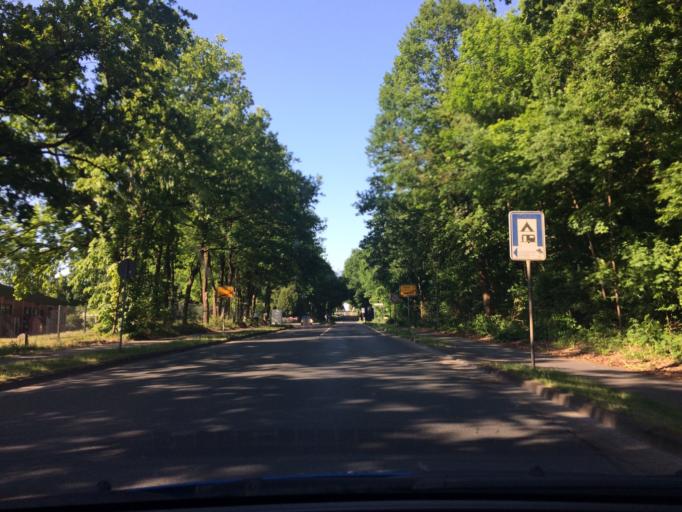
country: DE
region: Lower Saxony
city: Soltau
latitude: 52.9992
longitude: 9.8381
